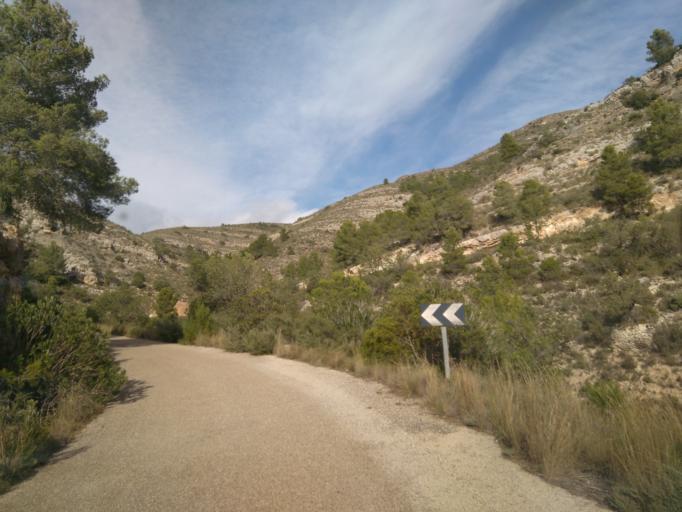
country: ES
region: Valencia
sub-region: Provincia de Valencia
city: Sumacarcer
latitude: 39.1537
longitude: -0.6513
